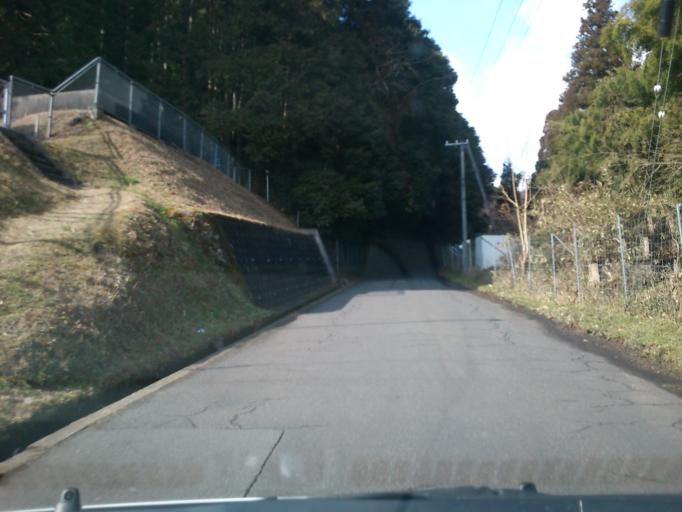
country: JP
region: Kyoto
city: Miyazu
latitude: 35.5805
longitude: 135.1777
